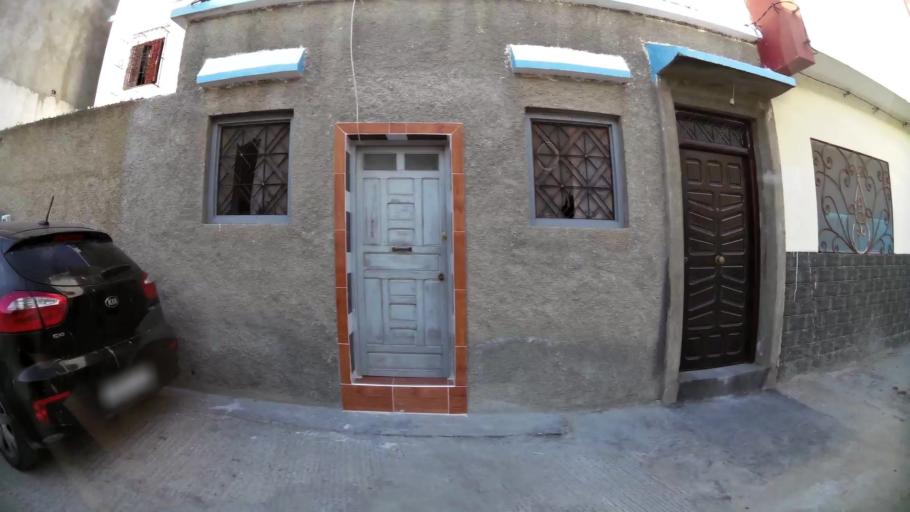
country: MA
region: Tanger-Tetouan
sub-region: Tetouan
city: Martil
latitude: 35.6273
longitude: -5.2763
